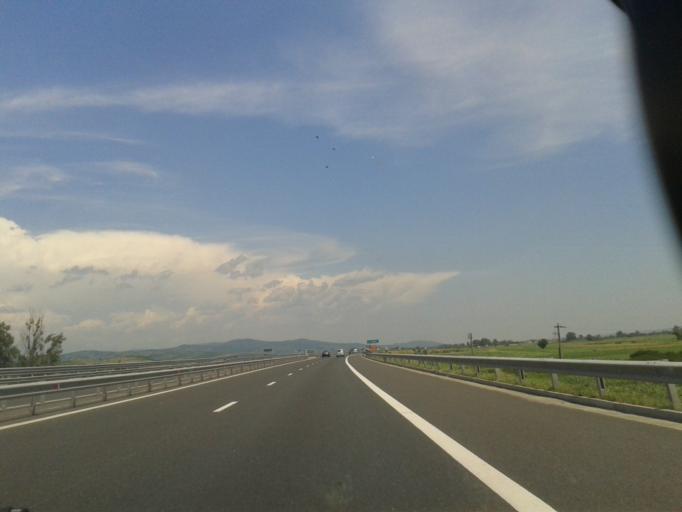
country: RO
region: Hunedoara
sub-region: Comuna Turdas
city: Pricaz
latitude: 45.8685
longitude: 23.1590
